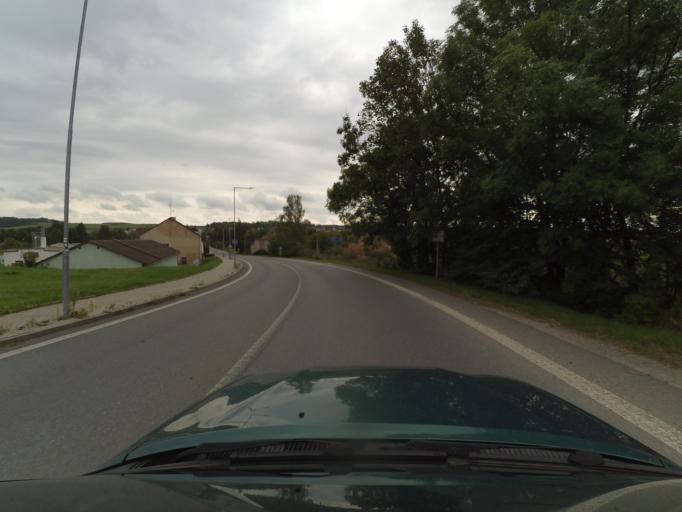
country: CZ
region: Plzensky
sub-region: Okres Plzen-Sever
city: Tremosna
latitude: 49.8194
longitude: 13.3926
